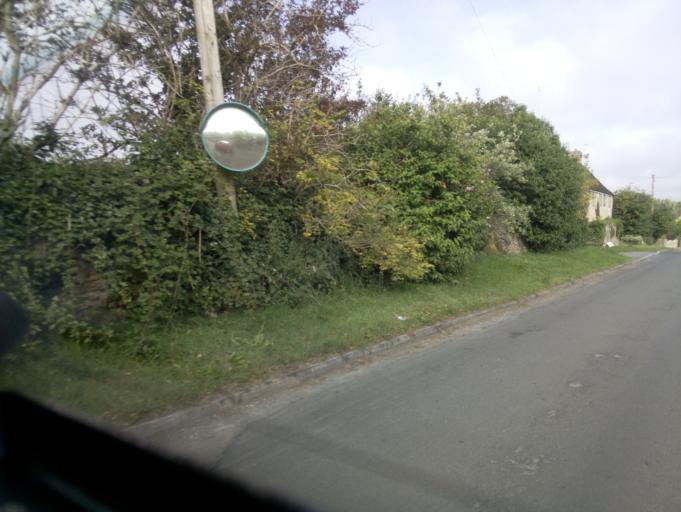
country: GB
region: England
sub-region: Borough of Swindon
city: Hannington
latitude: 51.6129
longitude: -1.7461
